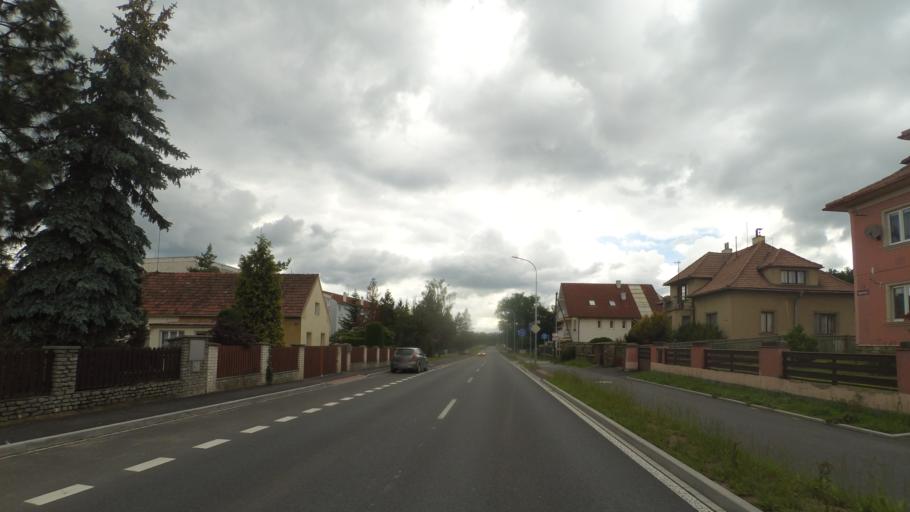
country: CZ
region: Plzensky
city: Horsovsky Tyn
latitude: 49.5330
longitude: 12.9319
